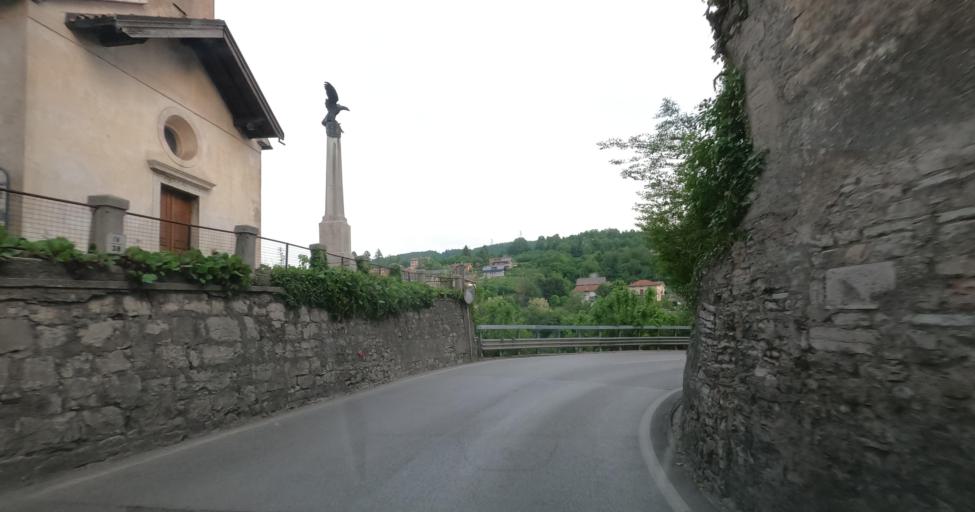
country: IT
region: Veneto
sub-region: Provincia di Belluno
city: Ponte nell'Alpi
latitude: 46.1735
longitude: 12.2841
